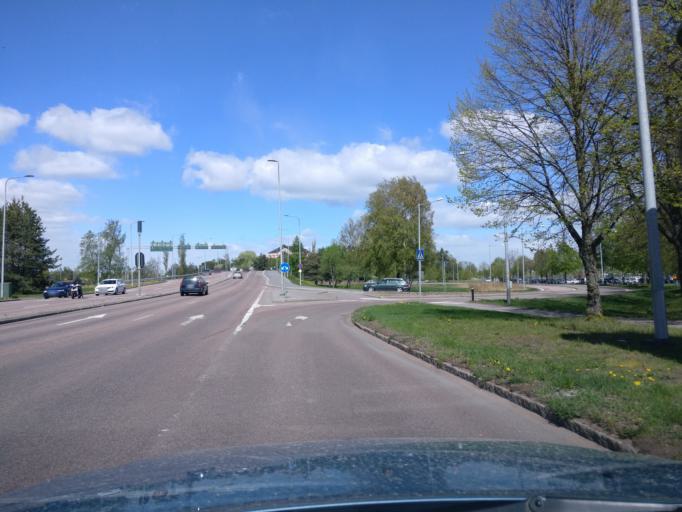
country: SE
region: Vaermland
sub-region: Karlstads Kommun
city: Karlstad
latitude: 59.3830
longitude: 13.4886
